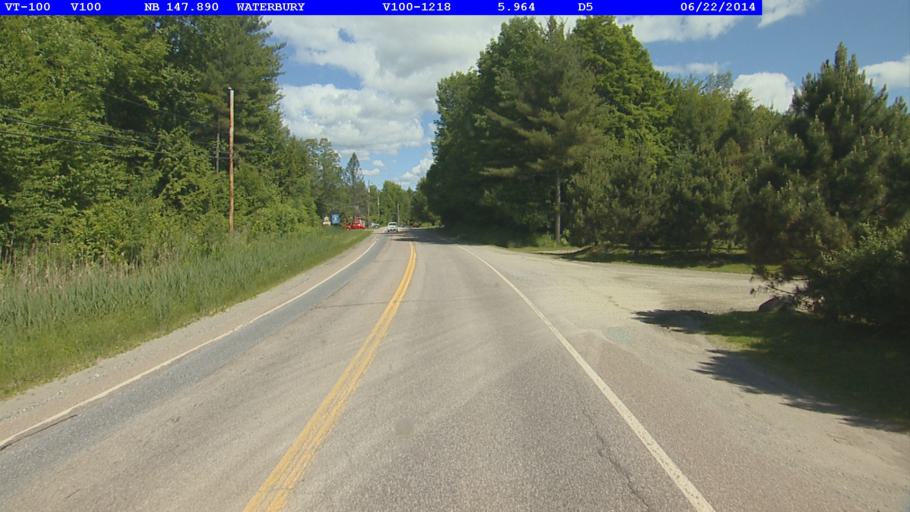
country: US
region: Vermont
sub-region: Washington County
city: Waterbury
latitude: 44.4144
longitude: -72.7215
